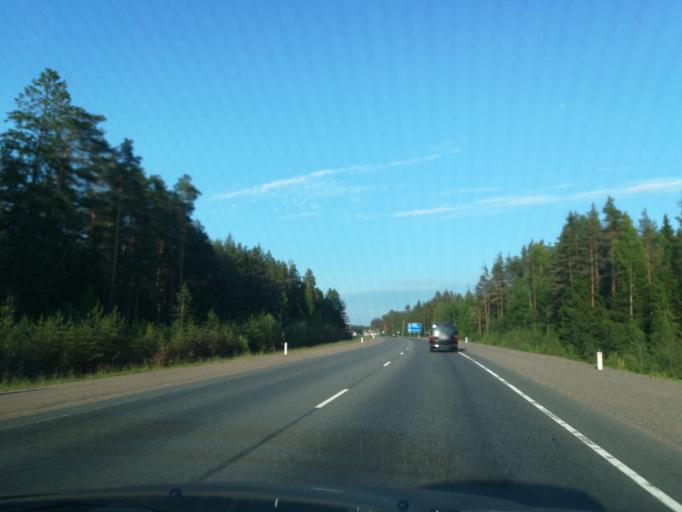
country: RU
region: Leningrad
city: Vyborg
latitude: 60.6690
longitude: 28.8914
